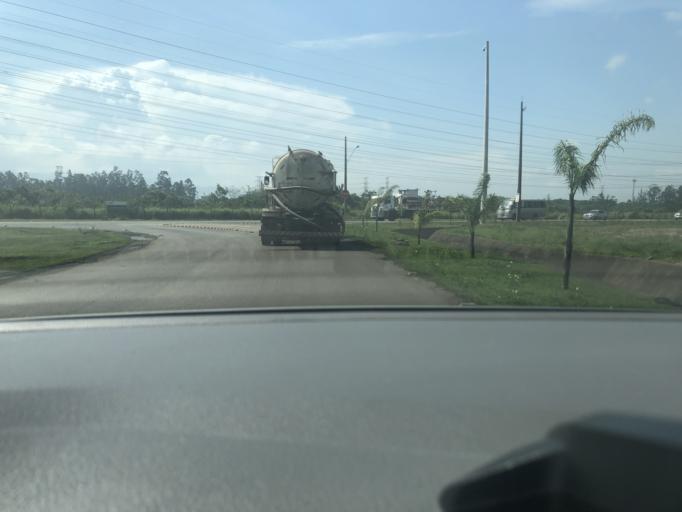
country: BR
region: Rio de Janeiro
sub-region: Itaguai
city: Itaguai
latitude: -22.9127
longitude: -43.7473
